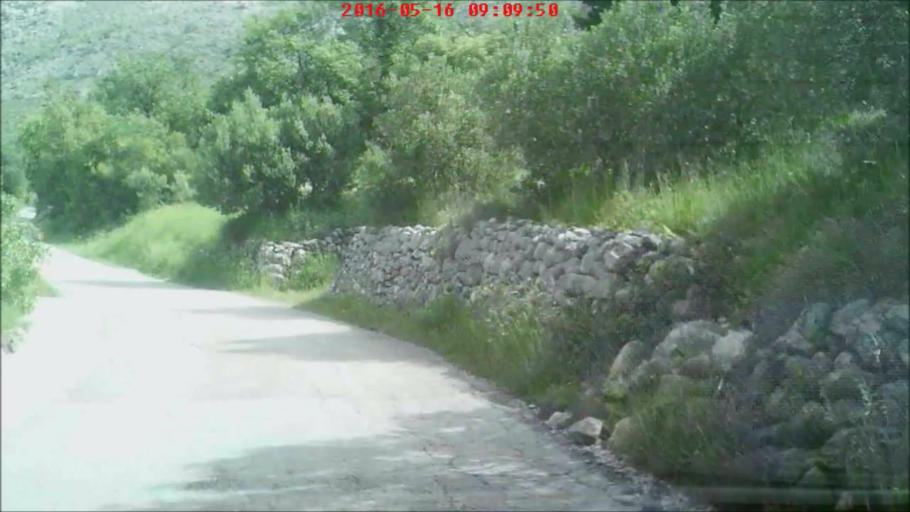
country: HR
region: Dubrovacko-Neretvanska
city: Podgora
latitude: 42.8154
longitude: 17.8560
